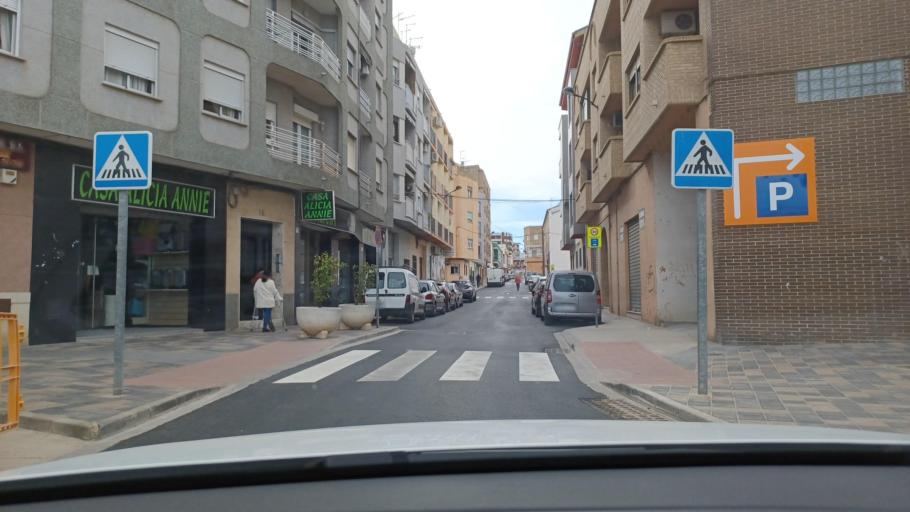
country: ES
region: Valencia
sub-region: Provincia de Valencia
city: Picassent
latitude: 39.3662
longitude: -0.4600
